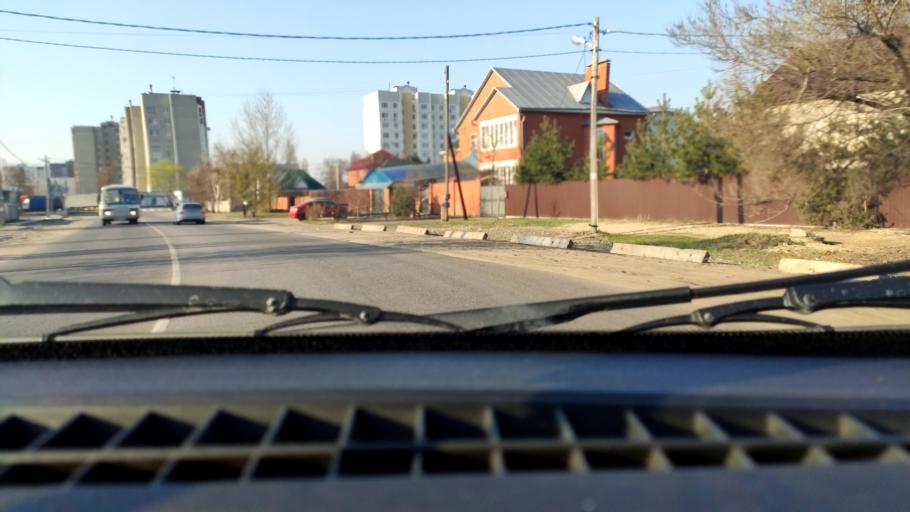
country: RU
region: Voronezj
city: Somovo
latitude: 51.7406
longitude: 39.2924
